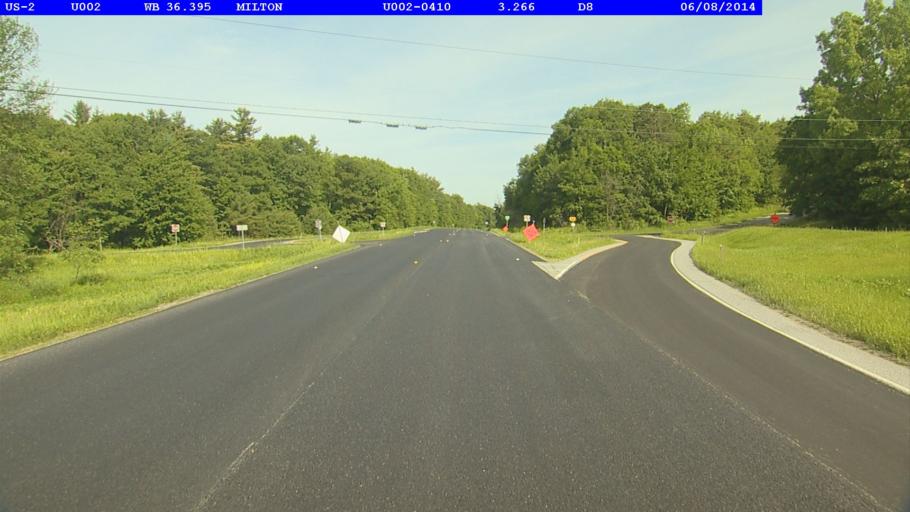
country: US
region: Vermont
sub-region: Chittenden County
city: Colchester
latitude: 44.6090
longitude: -73.2083
